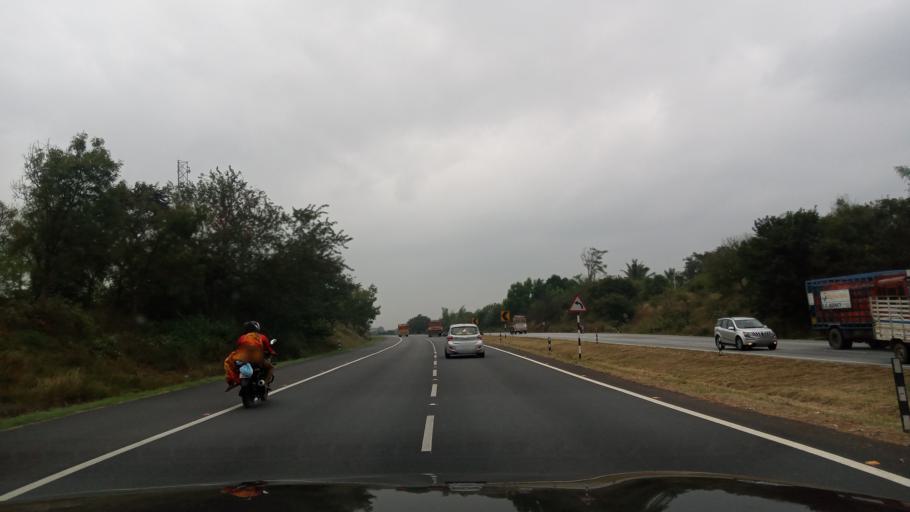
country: IN
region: Karnataka
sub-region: Bangalore Rural
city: Nelamangala
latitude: 13.0082
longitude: 77.4749
